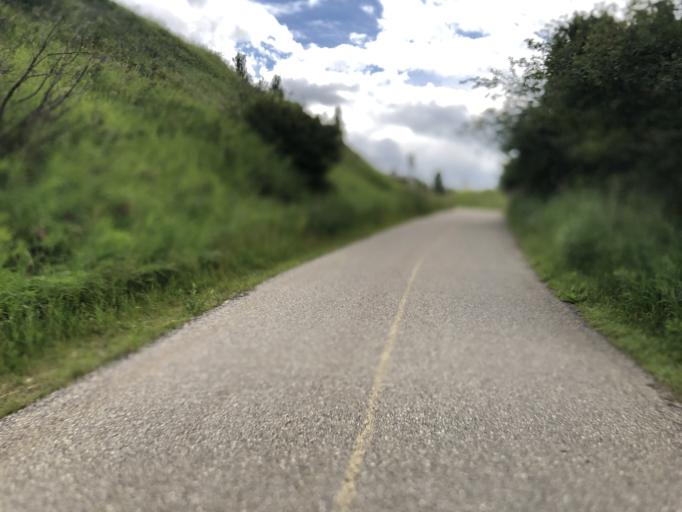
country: CA
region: Alberta
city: Calgary
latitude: 50.9986
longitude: -114.0229
